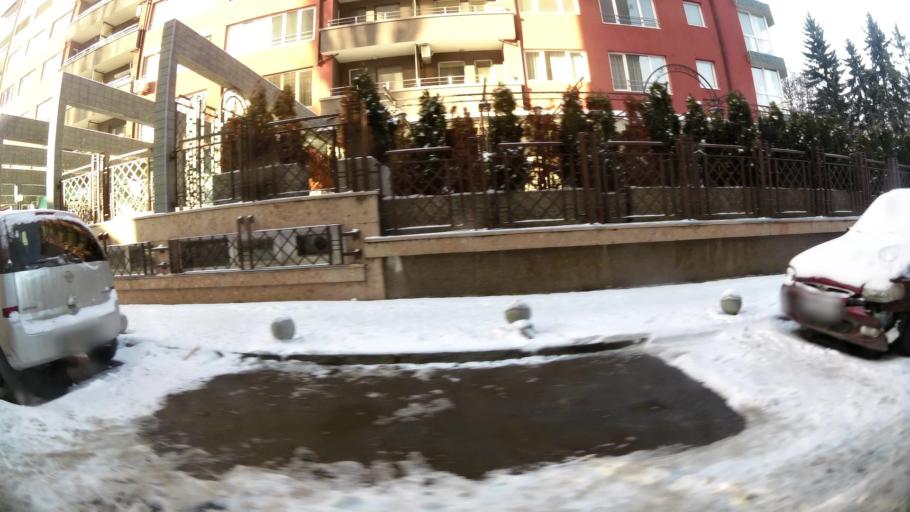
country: BG
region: Sofia-Capital
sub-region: Stolichna Obshtina
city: Sofia
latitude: 42.6687
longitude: 23.3469
